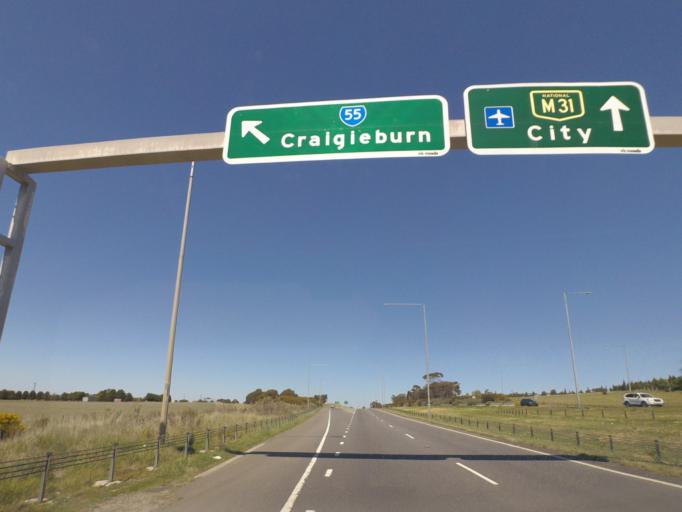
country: AU
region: Victoria
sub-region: Hume
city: Craigieburn
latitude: -37.5660
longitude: 144.9416
